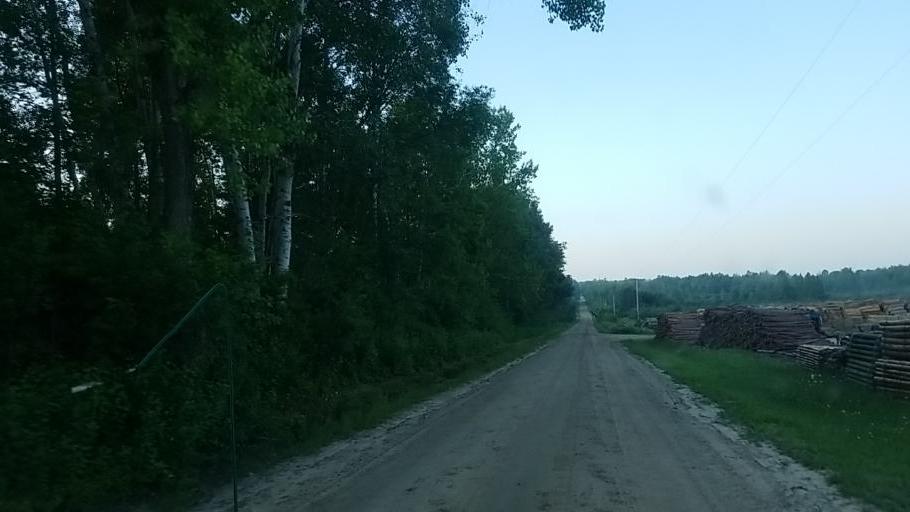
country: US
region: Michigan
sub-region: Osceola County
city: Evart
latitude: 43.9111
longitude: -85.1680
